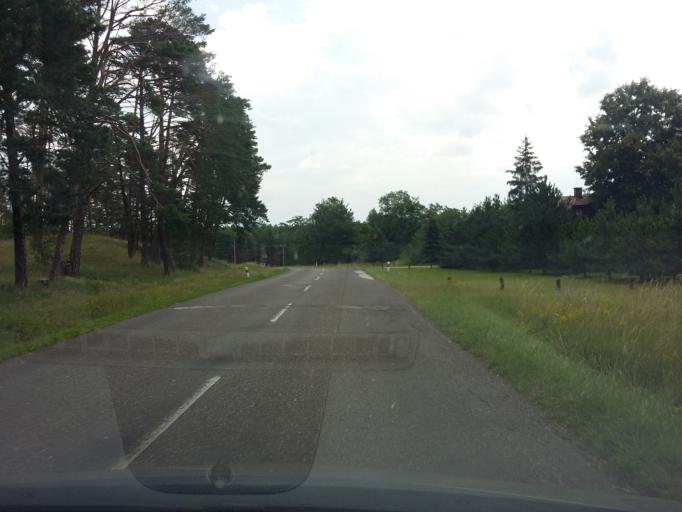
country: SK
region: Bratislavsky
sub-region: Okres Malacky
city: Malacky
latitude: 48.4604
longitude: 17.1459
